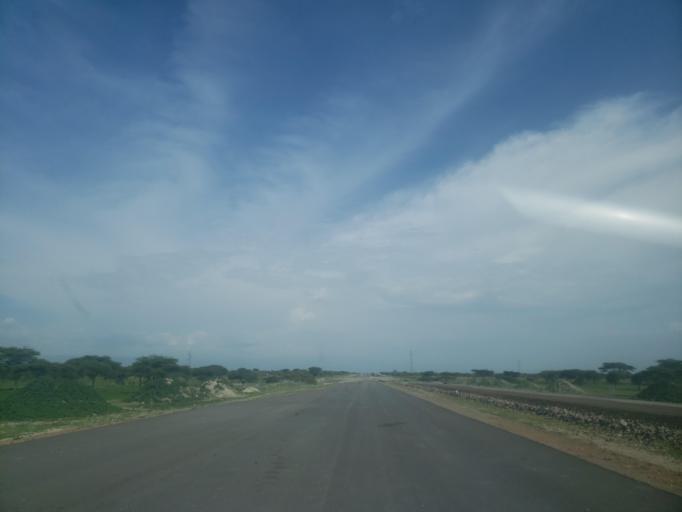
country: ET
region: Oromiya
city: Ziway
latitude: 7.6858
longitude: 38.6692
